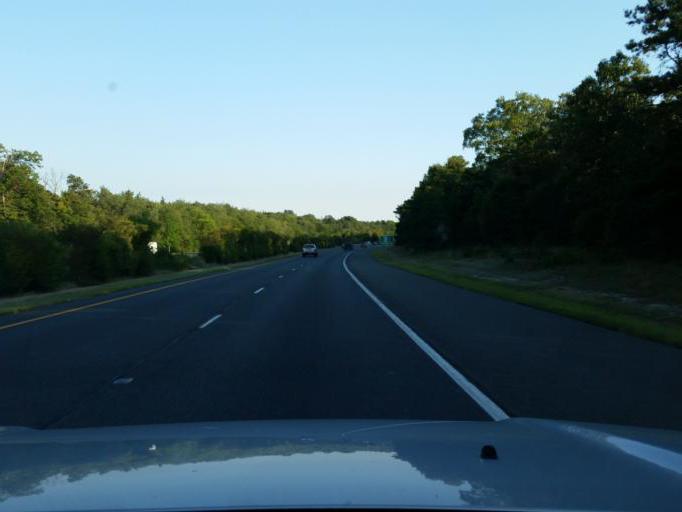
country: US
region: New Jersey
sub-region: Gloucester County
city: Newfield
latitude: 39.5709
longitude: -75.0646
